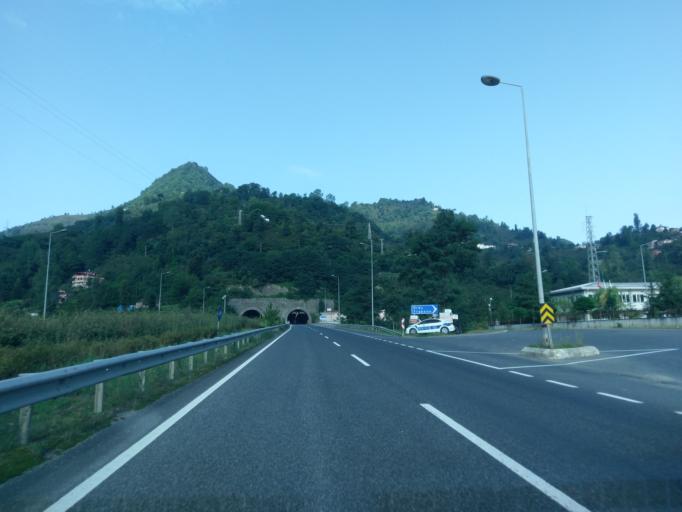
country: TR
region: Ordu
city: Persembe
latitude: 40.9842
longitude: 37.7096
